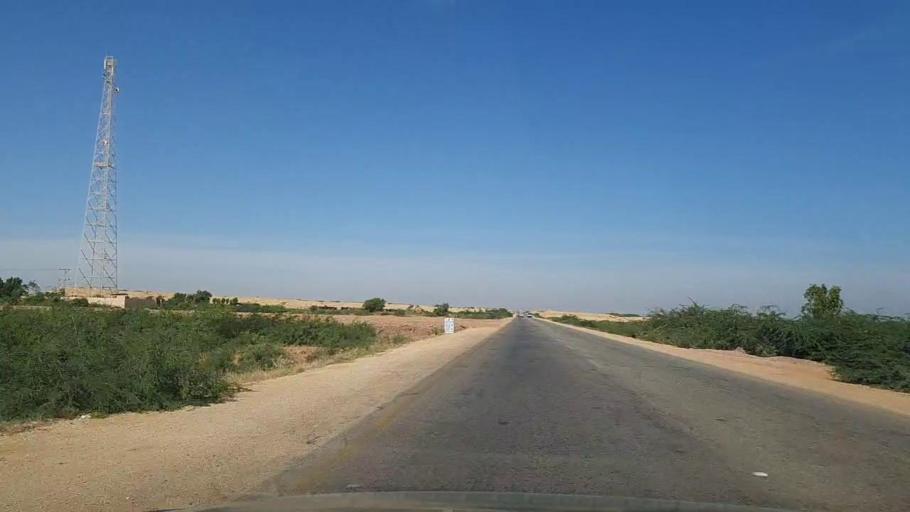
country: PK
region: Sindh
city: Kotri
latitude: 25.2053
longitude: 68.2375
